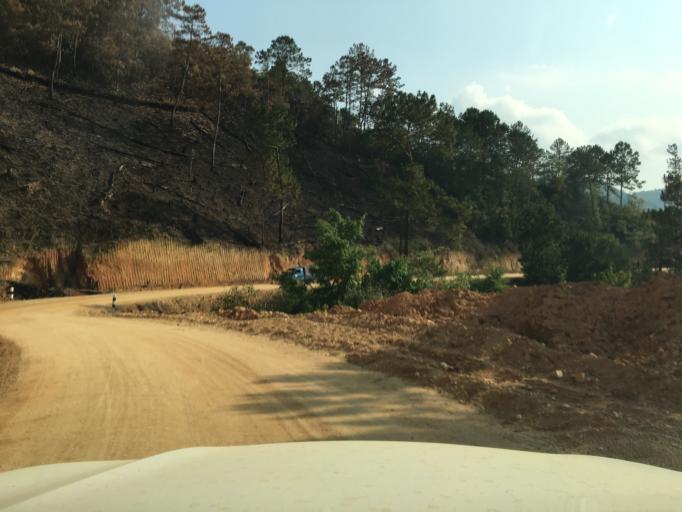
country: LA
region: Houaphan
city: Huameung
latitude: 20.1996
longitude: 103.8317
